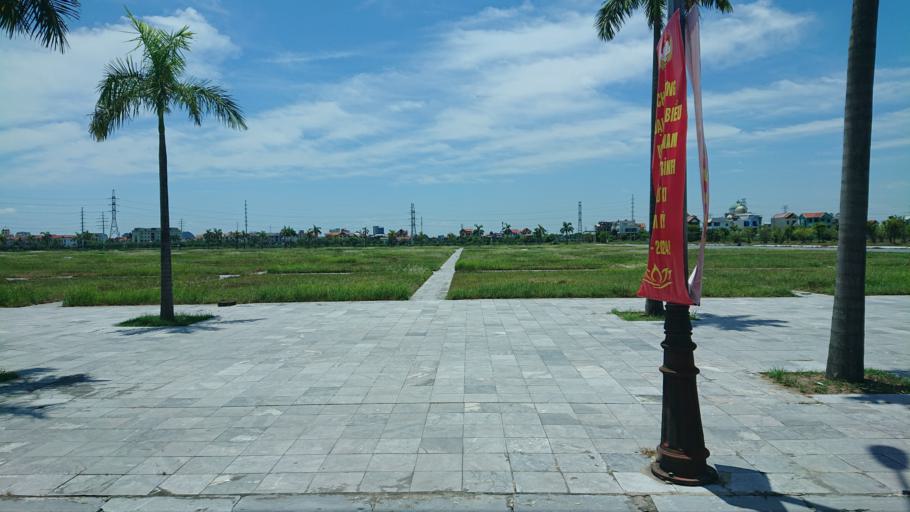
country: VN
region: Ninh Binh
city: Thanh Pho Ninh Binh
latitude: 20.2713
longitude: 105.9747
